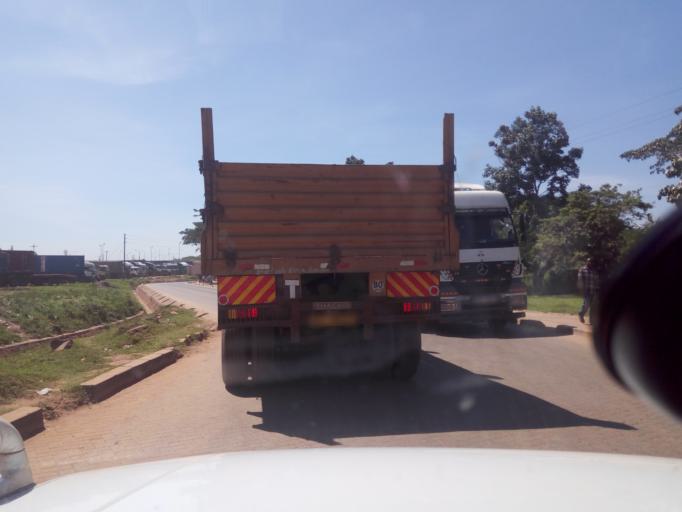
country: KE
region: Busia
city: Malaba
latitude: 0.6398
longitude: 34.2607
